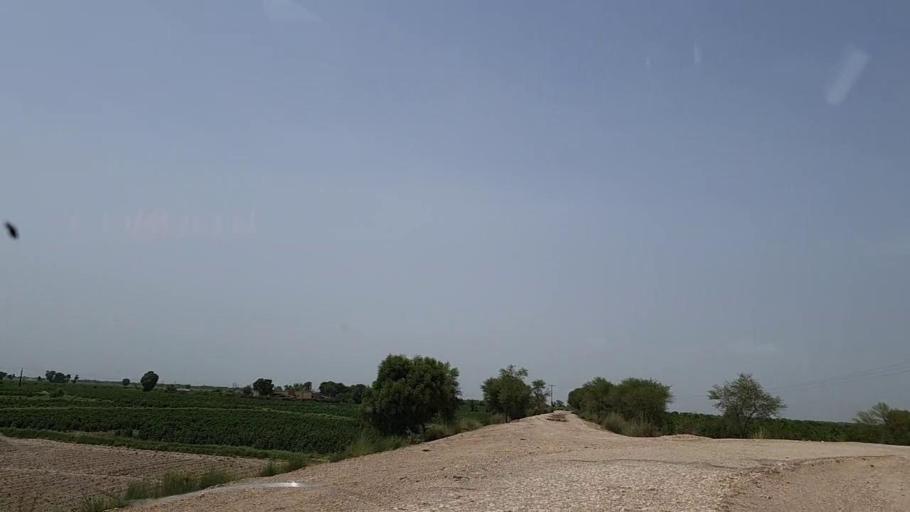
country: PK
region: Sindh
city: Tharu Shah
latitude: 27.0387
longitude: 68.1099
